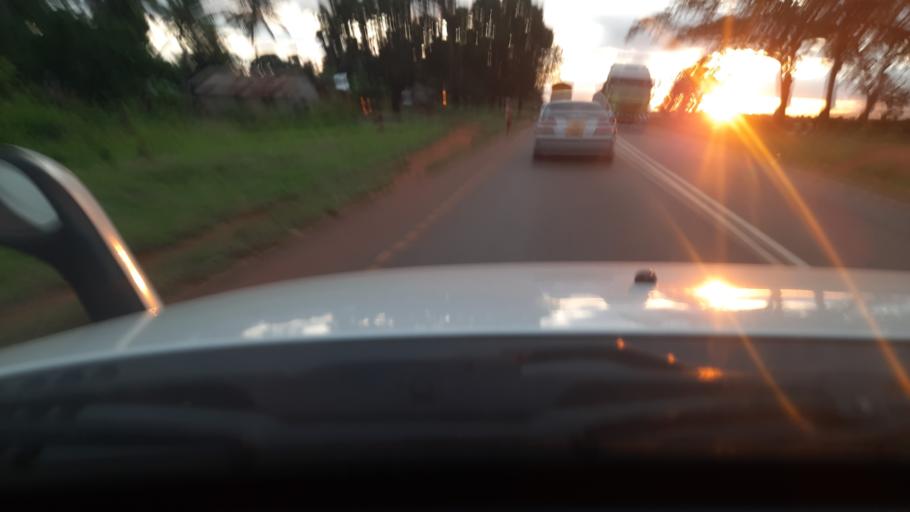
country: TZ
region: Tanga
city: Muheza
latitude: -5.1428
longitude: 38.8628
